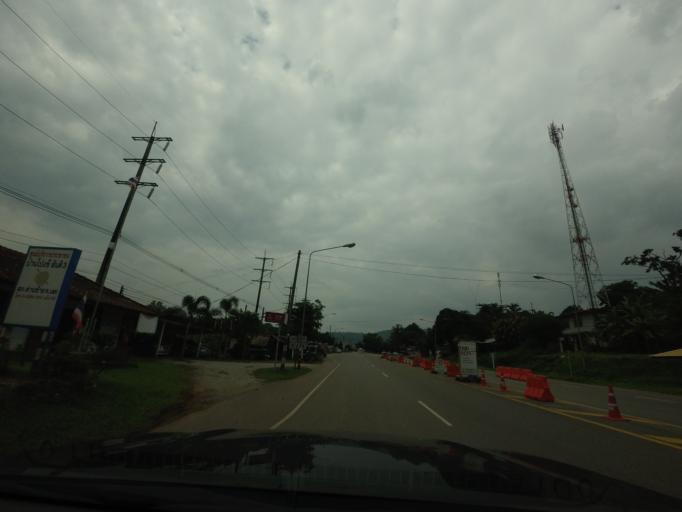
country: TH
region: Loei
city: Dan Sai
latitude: 17.2042
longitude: 101.1596
